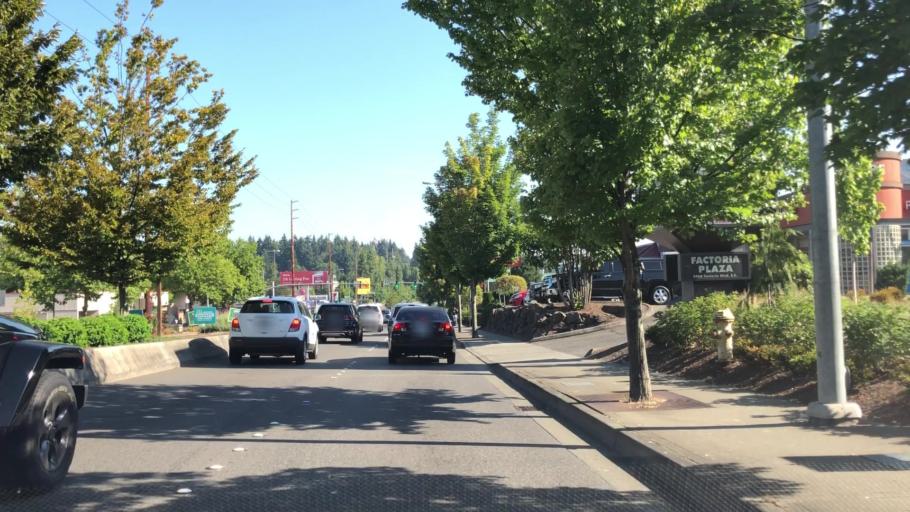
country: US
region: Washington
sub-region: King County
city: Newport
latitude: 47.5750
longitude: -122.1693
